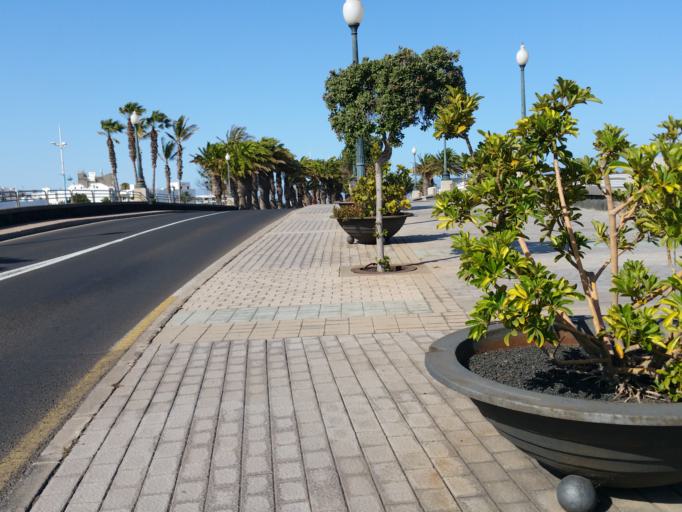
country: ES
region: Canary Islands
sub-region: Provincia de Las Palmas
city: Arrecife
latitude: 28.9599
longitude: -13.5457
